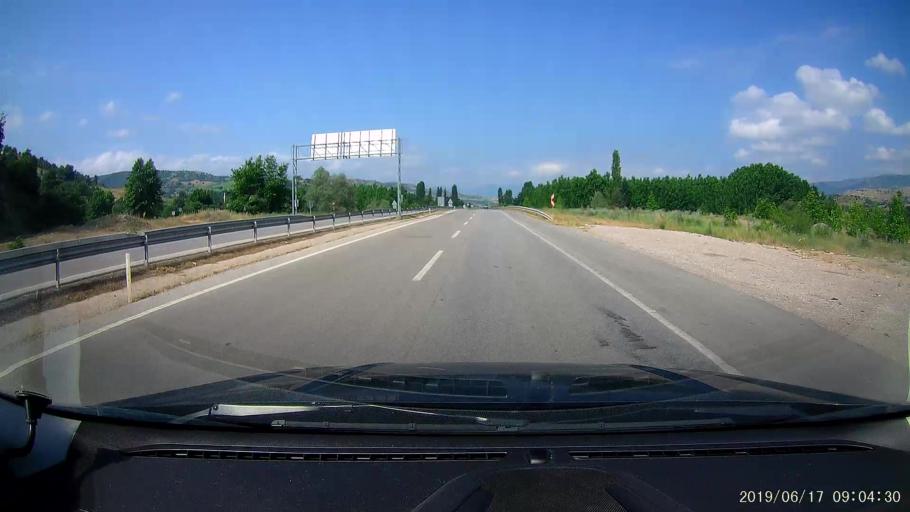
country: TR
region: Amasya
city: Tasova
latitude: 40.7450
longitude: 36.2868
